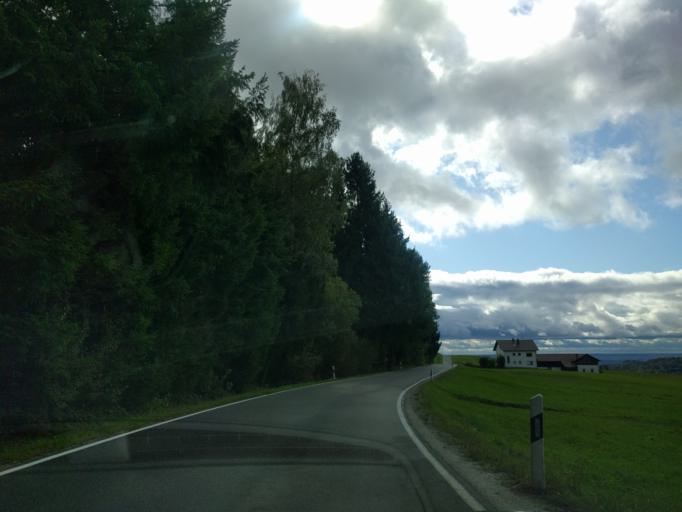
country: DE
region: Bavaria
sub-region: Lower Bavaria
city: Schaufling
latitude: 48.8299
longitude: 13.0568
